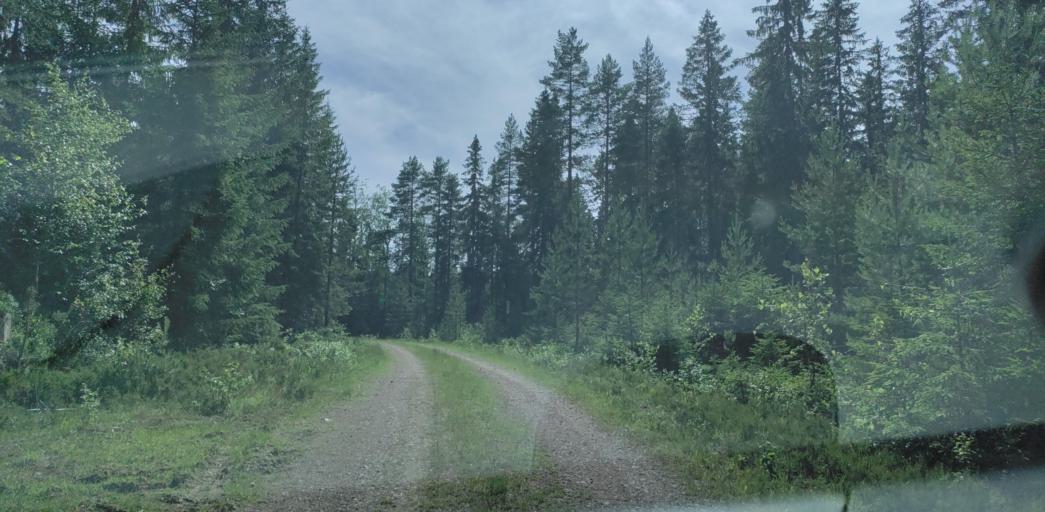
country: SE
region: Vaermland
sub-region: Hagfors Kommun
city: Ekshaerad
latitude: 60.0910
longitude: 13.3763
